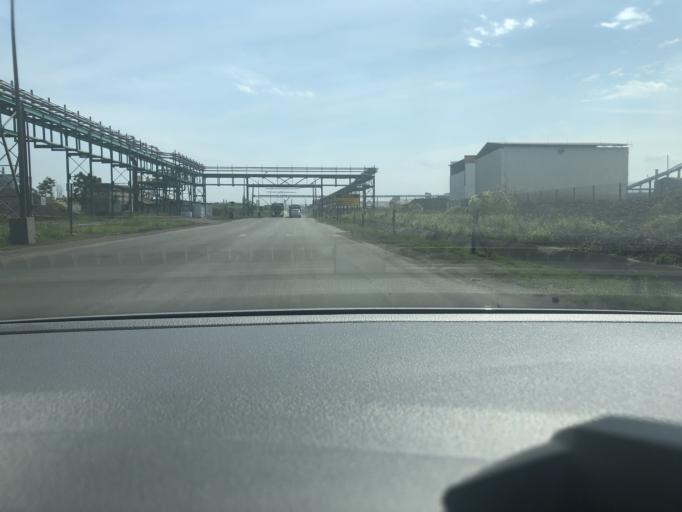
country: BR
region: Rio de Janeiro
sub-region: Itaguai
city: Itaguai
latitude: -22.9120
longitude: -43.7319
